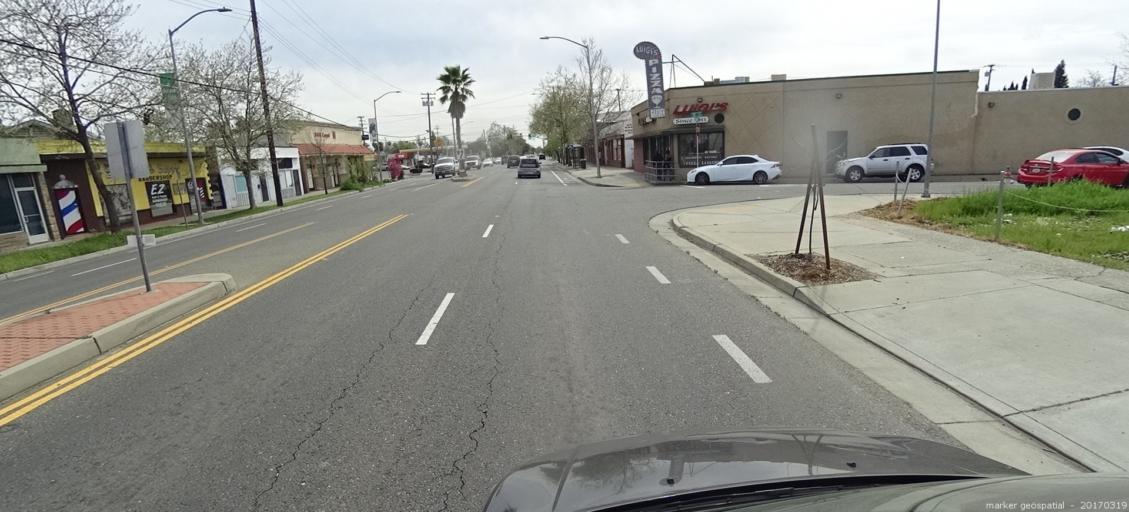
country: US
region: California
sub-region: Sacramento County
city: Parkway
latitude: 38.5406
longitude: -121.4505
